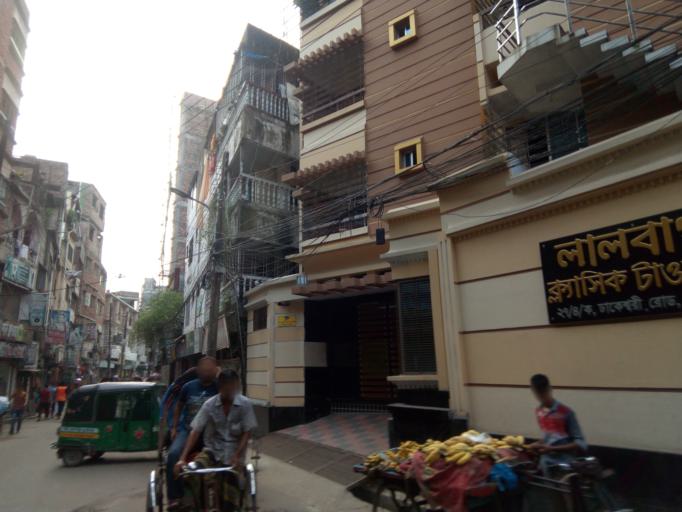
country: BD
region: Dhaka
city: Azimpur
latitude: 23.7209
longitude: 90.3889
